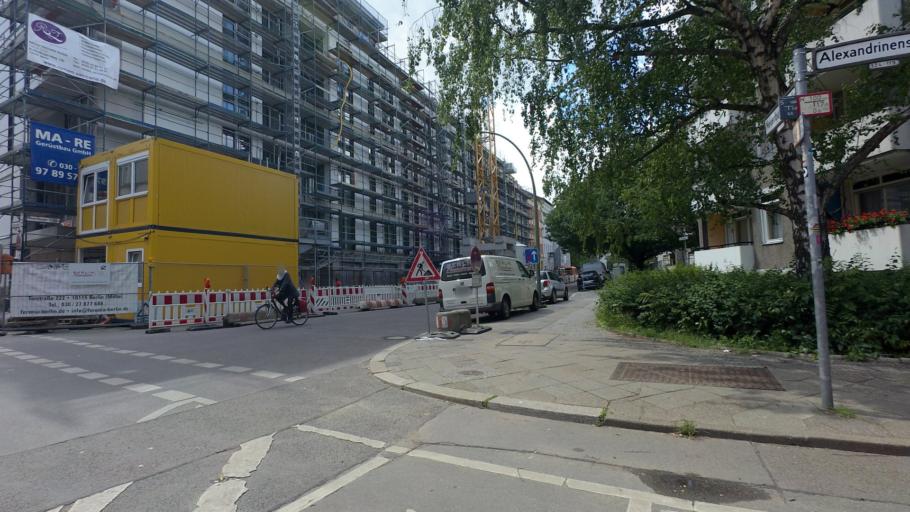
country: DE
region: Berlin
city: Bezirk Kreuzberg
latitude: 52.4996
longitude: 13.4004
